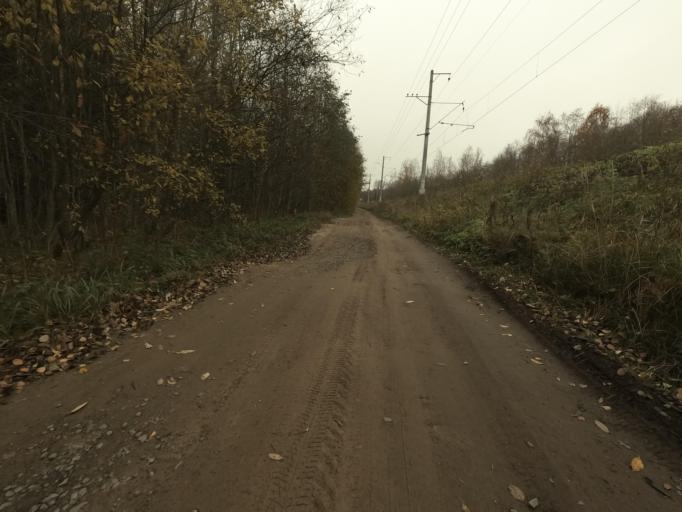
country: RU
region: Leningrad
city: Pavlovo
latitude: 59.7835
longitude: 30.8944
